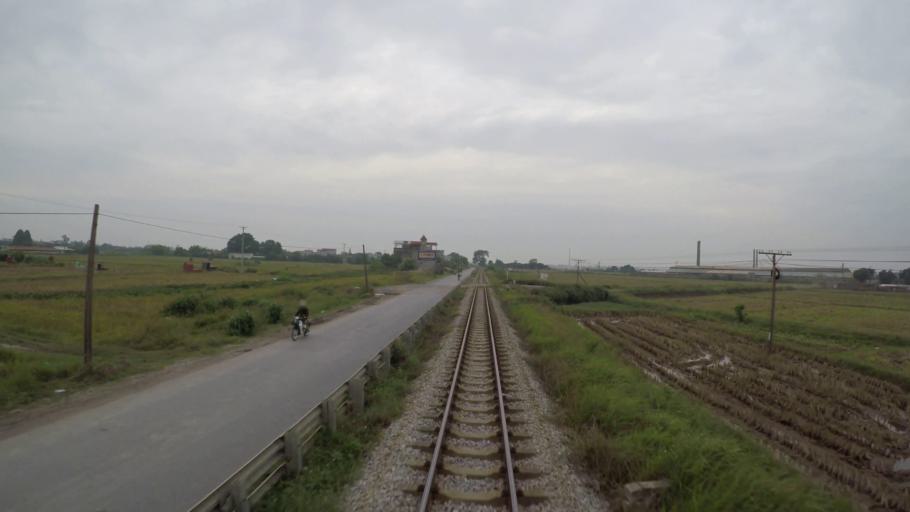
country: VN
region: Hung Yen
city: Ban Yen Nhan
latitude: 20.9705
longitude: 106.1009
